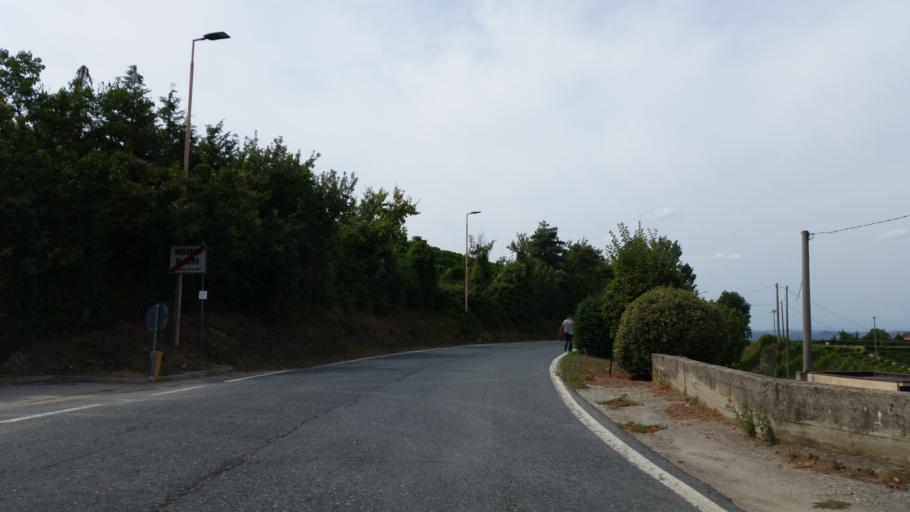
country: IT
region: Piedmont
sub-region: Provincia di Cuneo
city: Ricca
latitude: 44.6668
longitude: 8.0600
